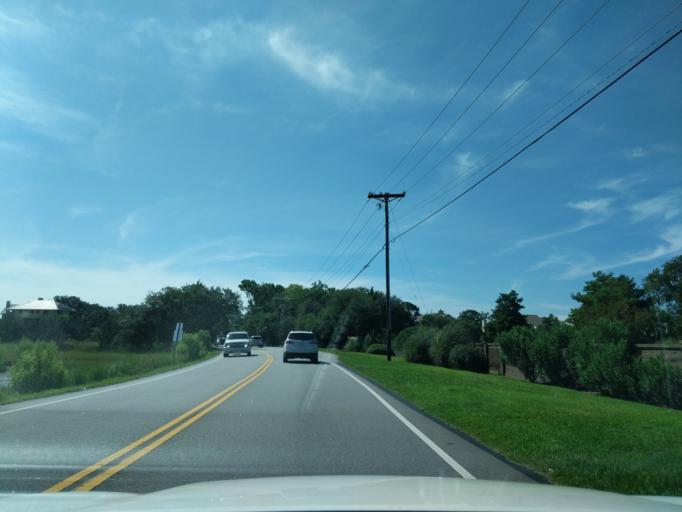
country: US
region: South Carolina
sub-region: Charleston County
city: Charleston
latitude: 32.7542
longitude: -79.9548
